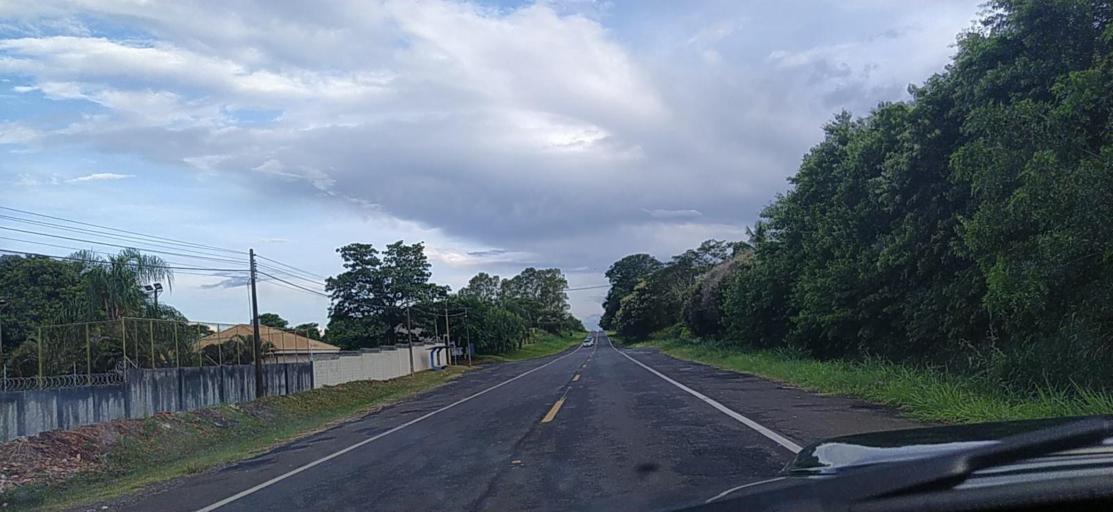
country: BR
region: Sao Paulo
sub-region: Pindorama
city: Pindorama
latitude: -21.1645
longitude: -48.9384
